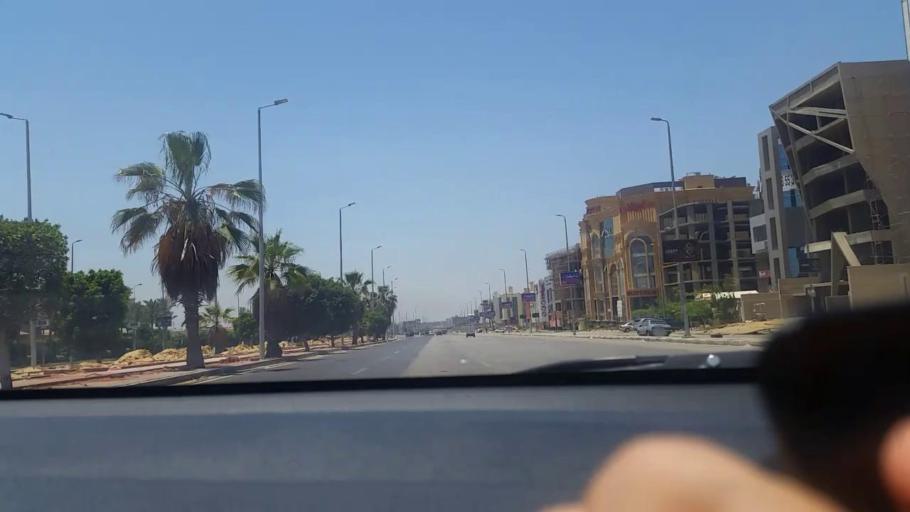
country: EG
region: Muhafazat al Qalyubiyah
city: Al Khankah
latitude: 30.0248
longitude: 31.4875
